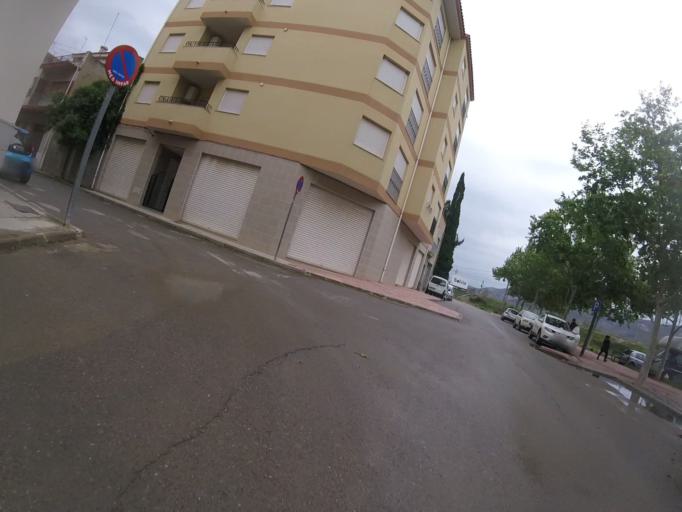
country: ES
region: Valencia
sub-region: Provincia de Castello
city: Alcala de Xivert
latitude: 40.3014
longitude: 0.2272
